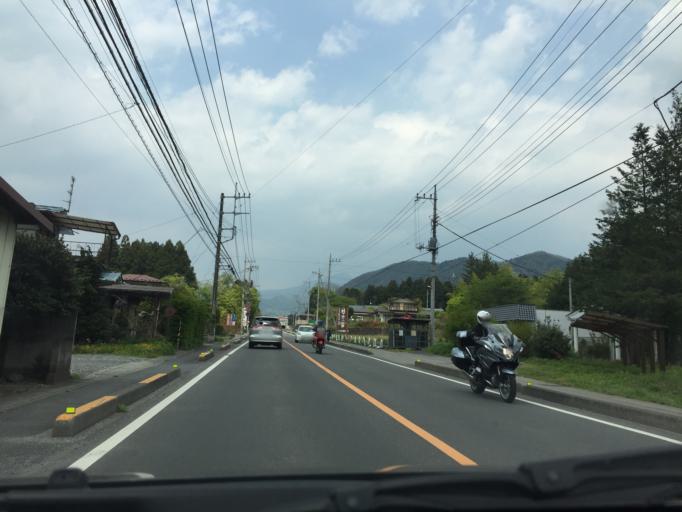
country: JP
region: Tochigi
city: Imaichi
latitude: 36.8099
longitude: 139.7100
